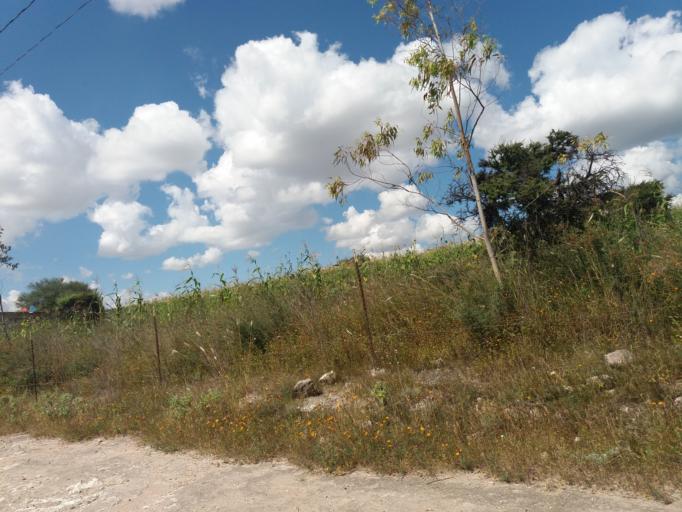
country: MX
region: Aguascalientes
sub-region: Aguascalientes
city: San Sebastian [Fraccionamiento]
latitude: 21.8089
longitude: -102.2417
